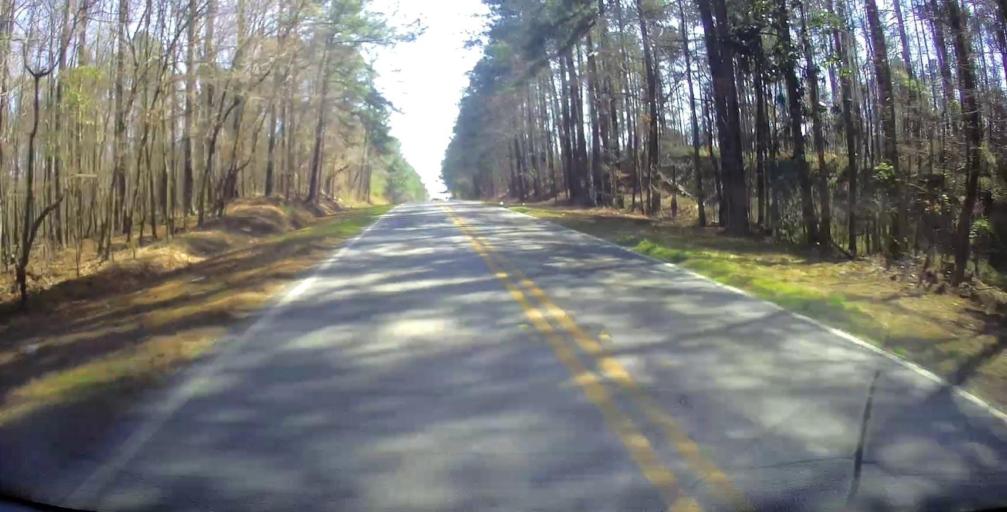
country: US
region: Georgia
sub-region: Jones County
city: Gray
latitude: 32.9246
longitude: -83.5315
